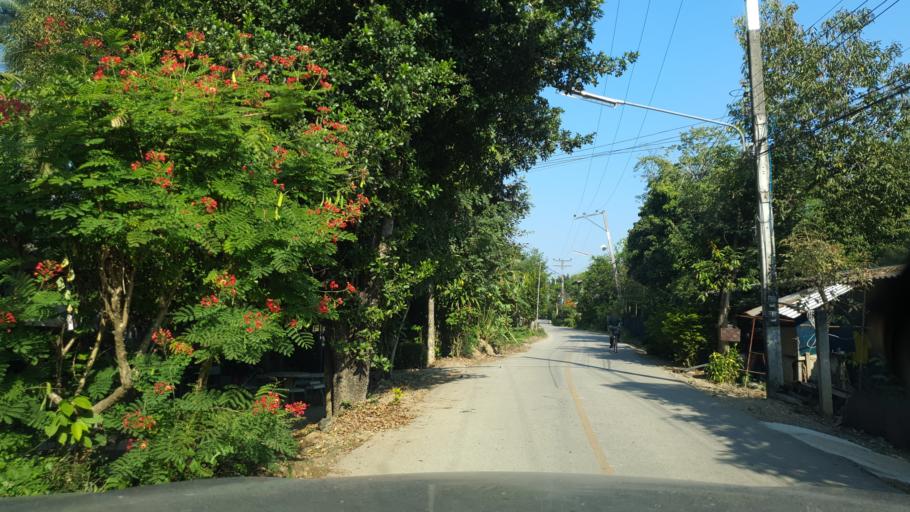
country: TH
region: Chiang Mai
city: Saraphi
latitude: 18.7084
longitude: 99.0748
